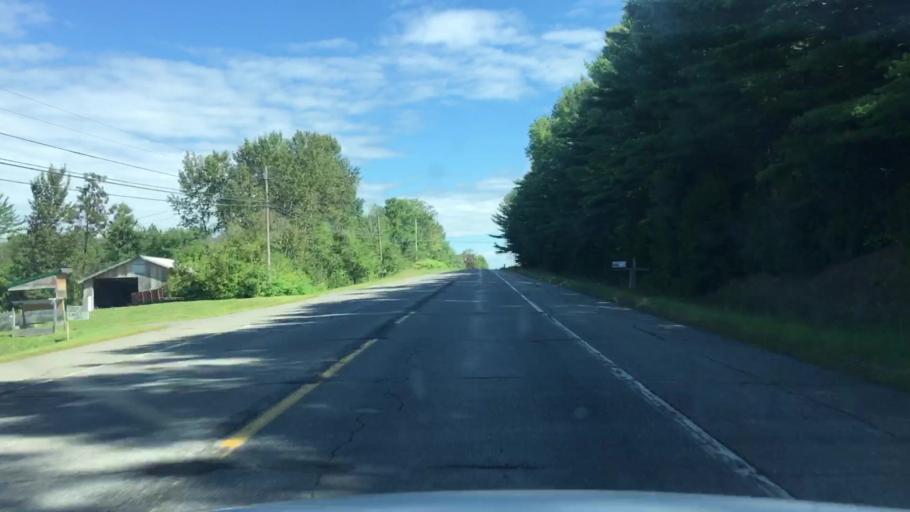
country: US
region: Maine
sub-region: Penobscot County
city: Dexter
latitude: 45.0579
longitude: -69.2533
